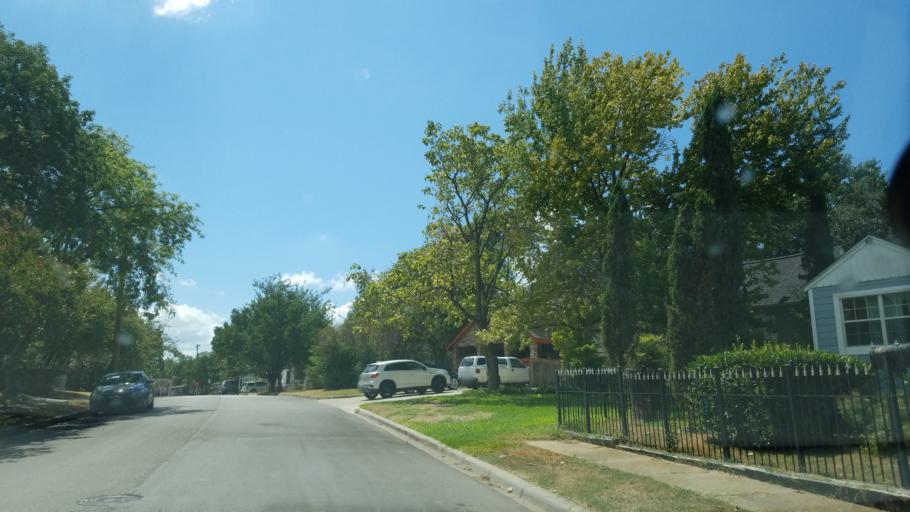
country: US
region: Texas
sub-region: Dallas County
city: Dallas
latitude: 32.7573
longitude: -96.8299
